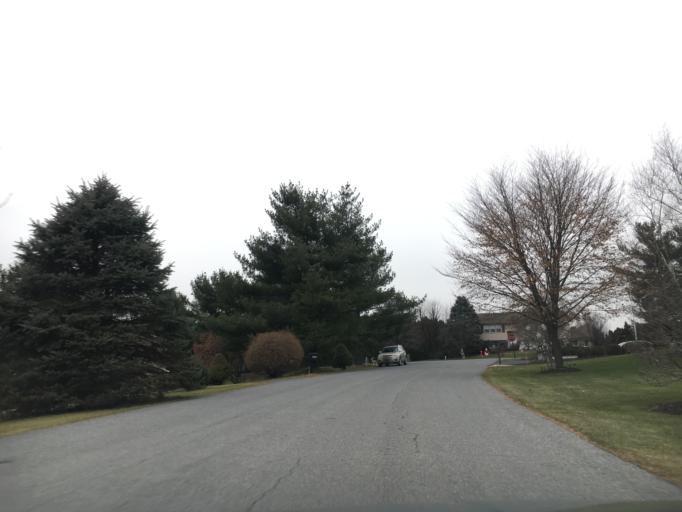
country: US
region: Pennsylvania
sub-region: Lehigh County
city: Schnecksville
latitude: 40.7025
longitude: -75.5800
